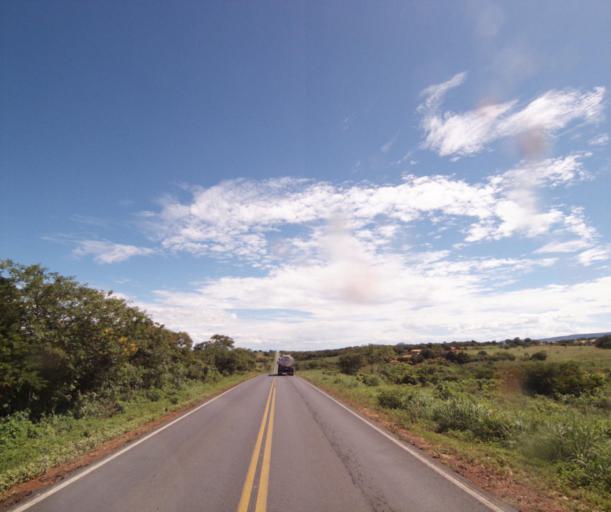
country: BR
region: Bahia
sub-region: Guanambi
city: Guanambi
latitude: -14.5230
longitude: -42.6954
